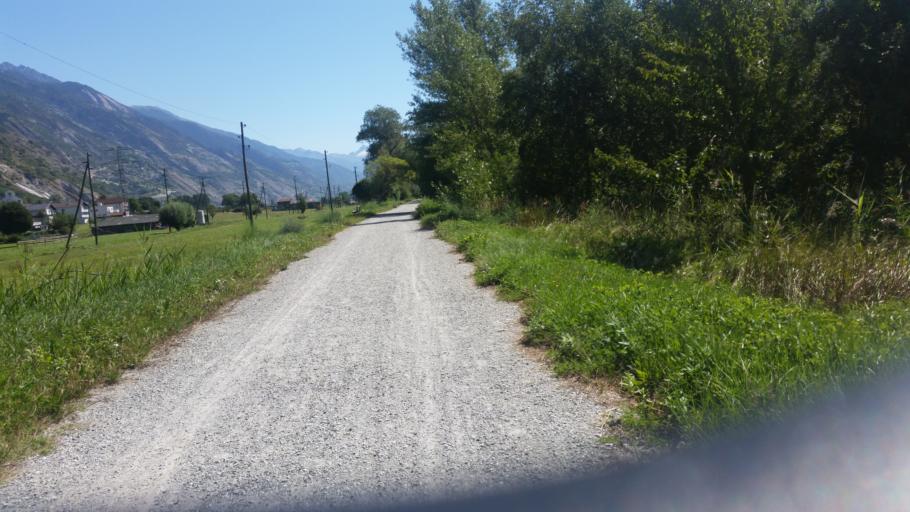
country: CH
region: Valais
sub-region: Leuk District
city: Turtmann
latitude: 46.3106
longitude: 7.7085
